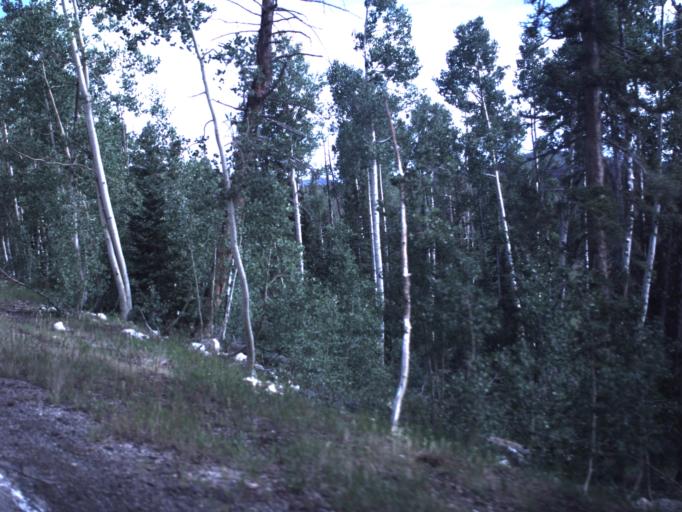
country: US
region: Utah
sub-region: Iron County
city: Parowan
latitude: 37.5349
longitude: -112.7728
